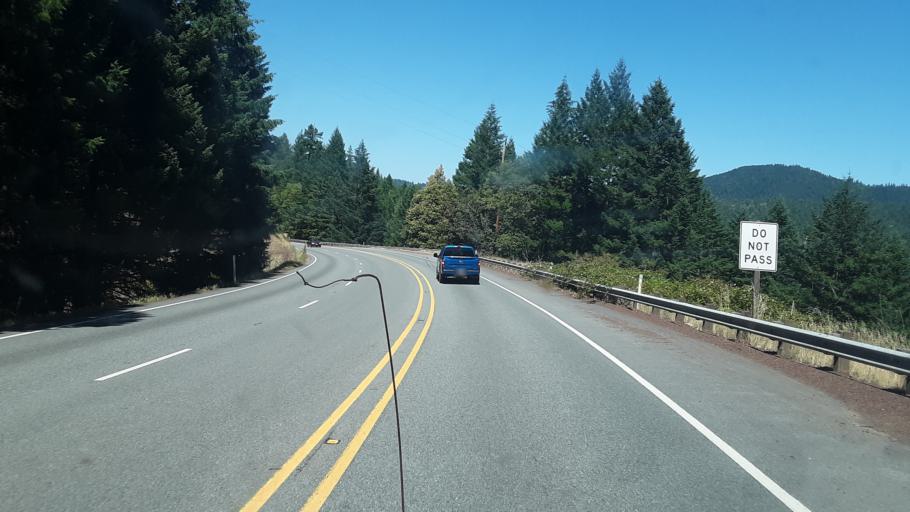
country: US
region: Oregon
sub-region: Josephine County
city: Cave Junction
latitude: 42.3348
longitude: -123.5846
